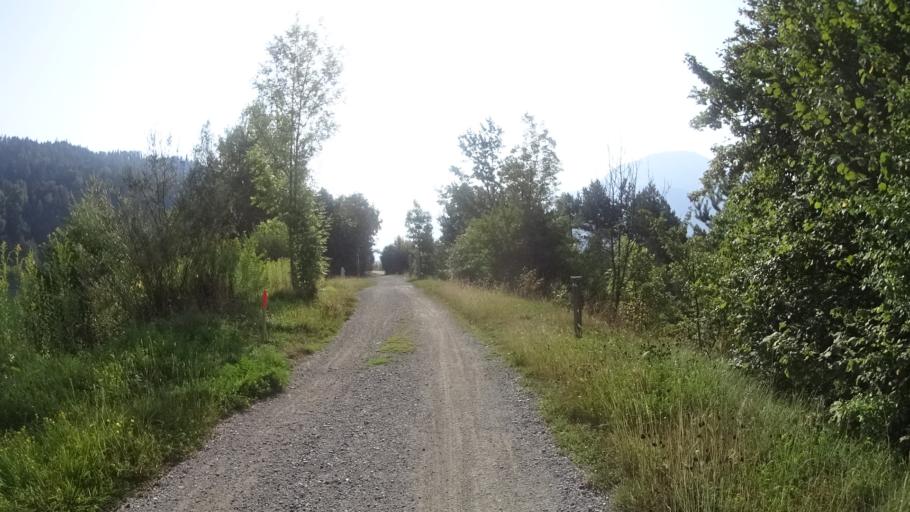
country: AT
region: Carinthia
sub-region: Politischer Bezirk Klagenfurt Land
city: Maria Rain
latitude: 46.5459
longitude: 14.2963
